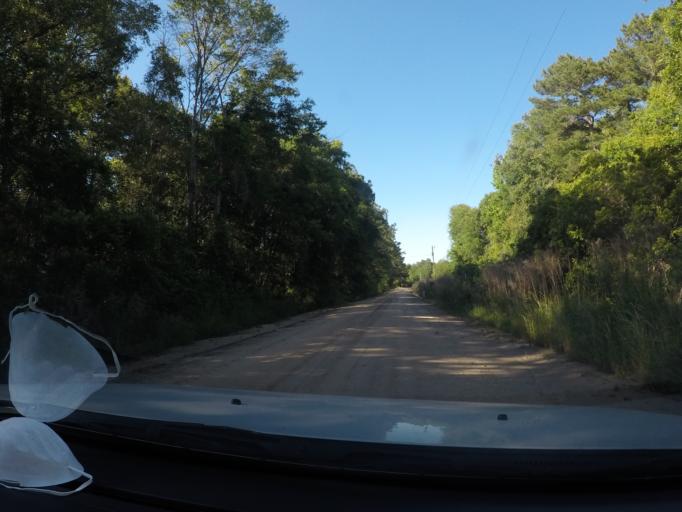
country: US
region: Georgia
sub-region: Bulloch County
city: Brooklet
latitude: 32.3046
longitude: -81.7478
